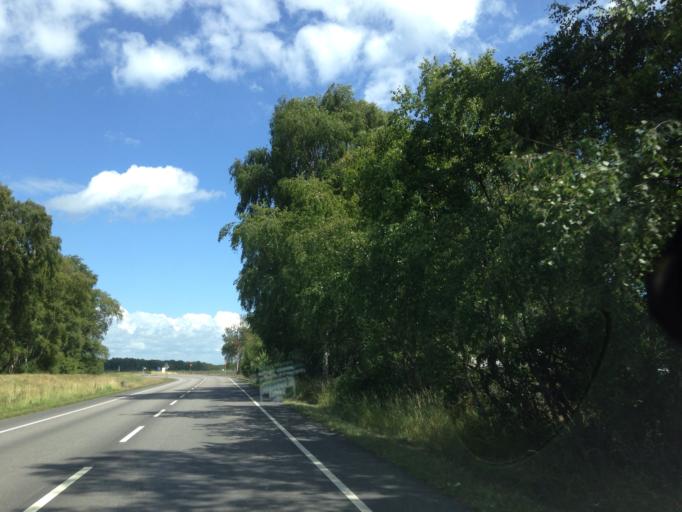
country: SE
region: Skane
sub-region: Vellinge Kommun
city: Skanor med Falsterbo
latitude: 55.3993
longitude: 12.8627
